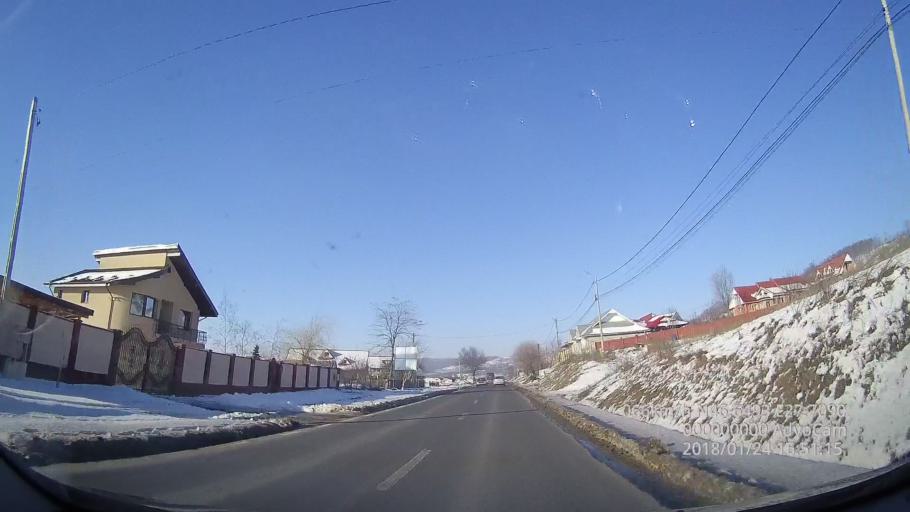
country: RO
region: Vaslui
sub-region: Municipiul Vaslui
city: Rediu
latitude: 46.6497
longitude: 27.7089
